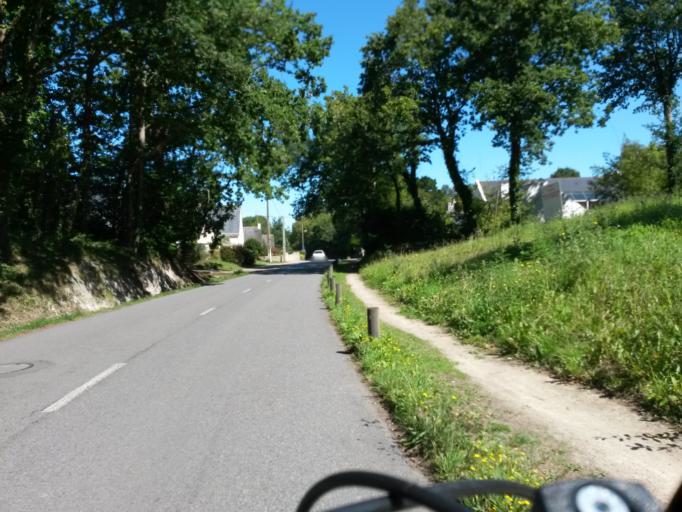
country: FR
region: Pays de la Loire
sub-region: Departement de la Loire-Atlantique
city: Mesquer
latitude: 47.3956
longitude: -2.4603
